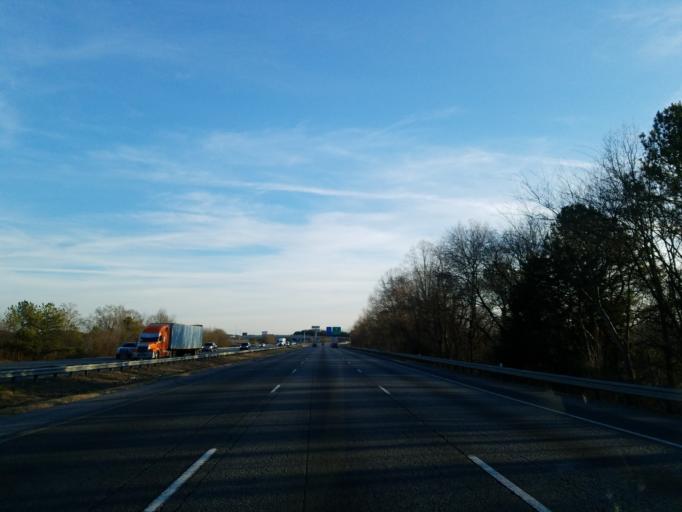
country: US
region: Georgia
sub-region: Gordon County
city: Calhoun
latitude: 34.5836
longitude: -84.9526
